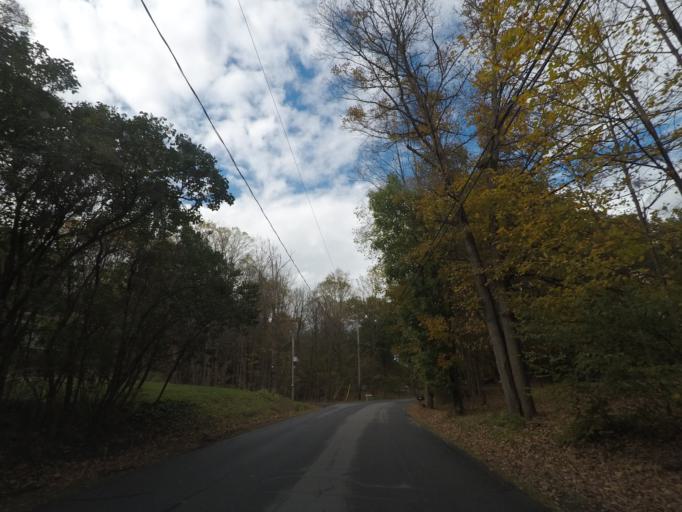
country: US
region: New York
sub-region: Rensselaer County
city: East Greenbush
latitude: 42.5792
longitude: -73.6637
